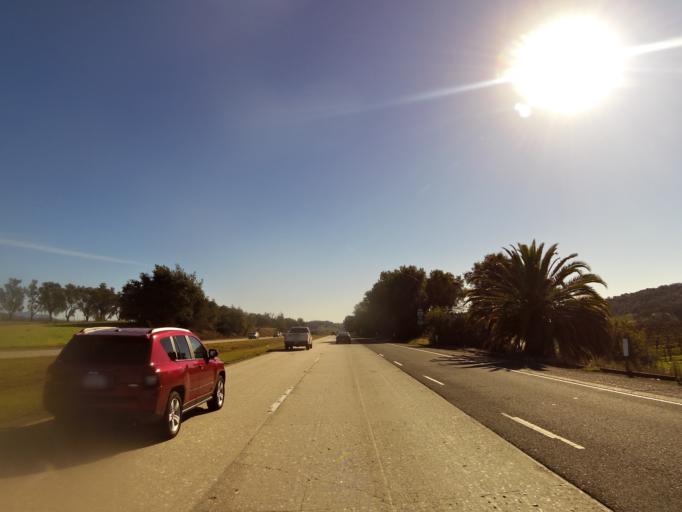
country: US
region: California
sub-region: Sonoma County
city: Cloverdale
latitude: 38.7567
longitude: -122.9725
